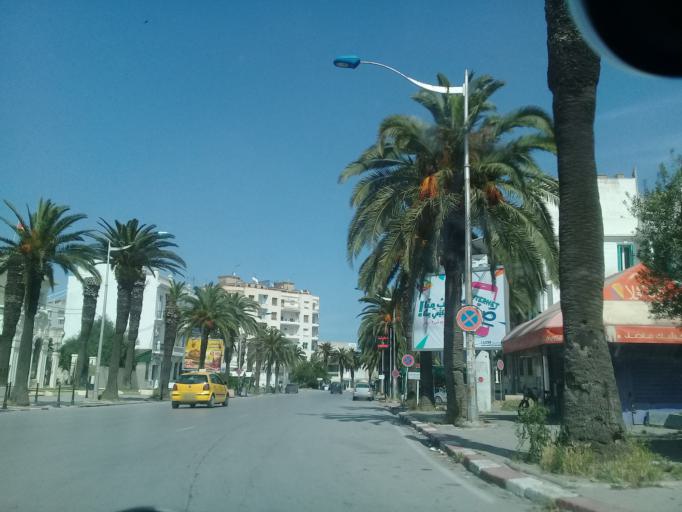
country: TN
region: Tunis
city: Tunis
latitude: 36.8209
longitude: 10.1786
